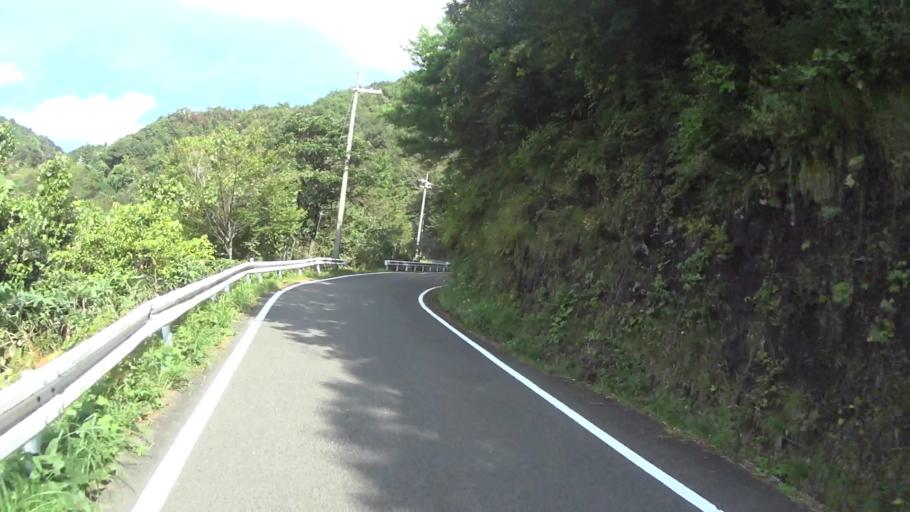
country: JP
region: Kyoto
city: Miyazu
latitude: 35.6775
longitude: 135.2660
